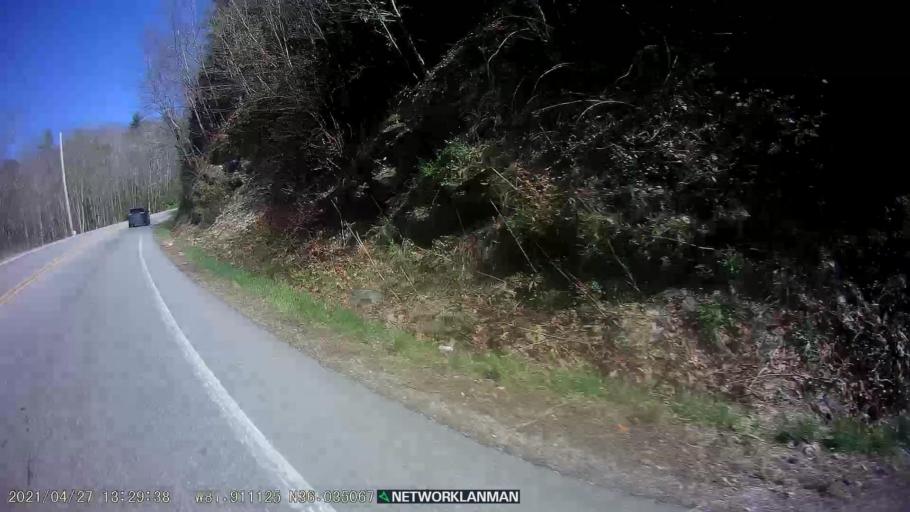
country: US
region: North Carolina
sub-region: Avery County
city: Newland
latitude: 36.0351
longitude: -81.9109
